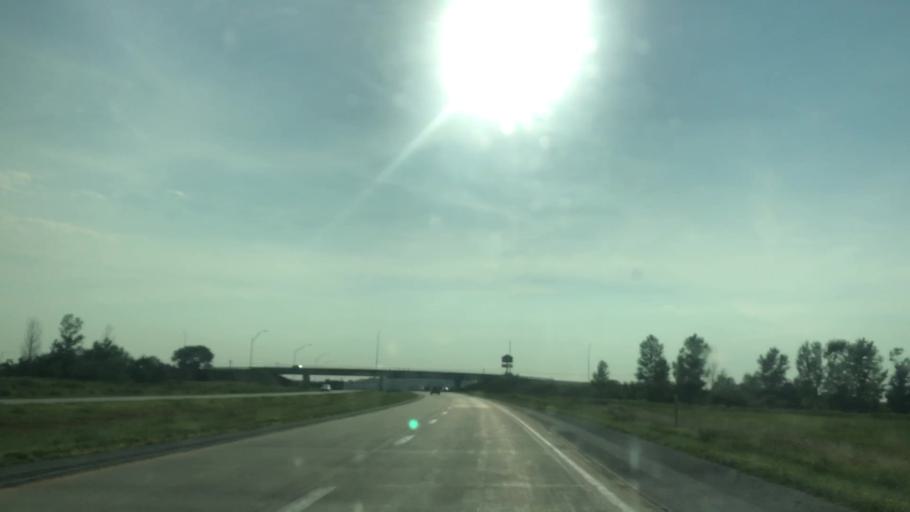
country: US
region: Iowa
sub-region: Story County
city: Nevada
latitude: 42.0082
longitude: -93.4311
